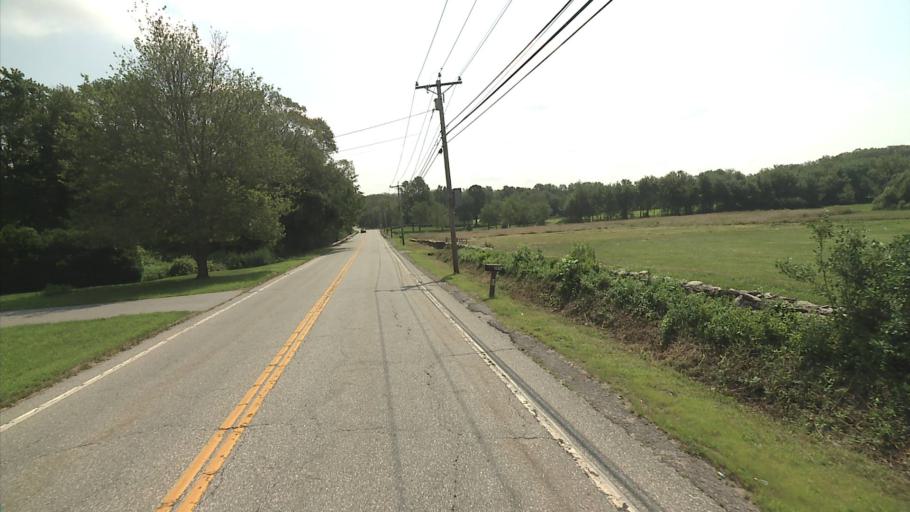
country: US
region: Connecticut
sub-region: New London County
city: Preston City
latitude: 41.5329
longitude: -72.0081
